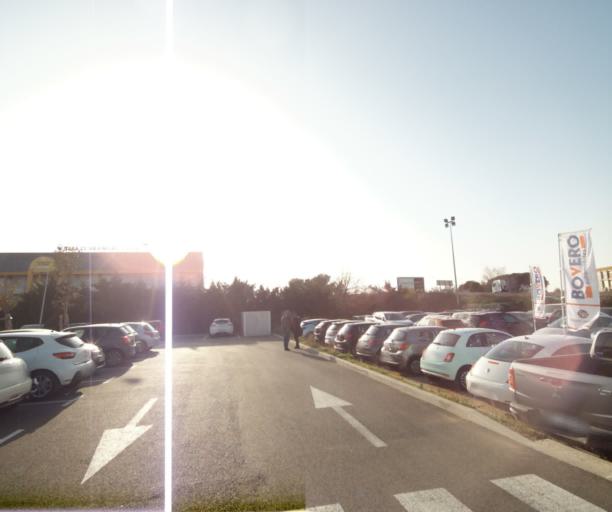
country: FR
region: Provence-Alpes-Cote d'Azur
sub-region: Departement des Bouches-du-Rhone
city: Saint-Victoret
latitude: 43.4260
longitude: 5.2524
